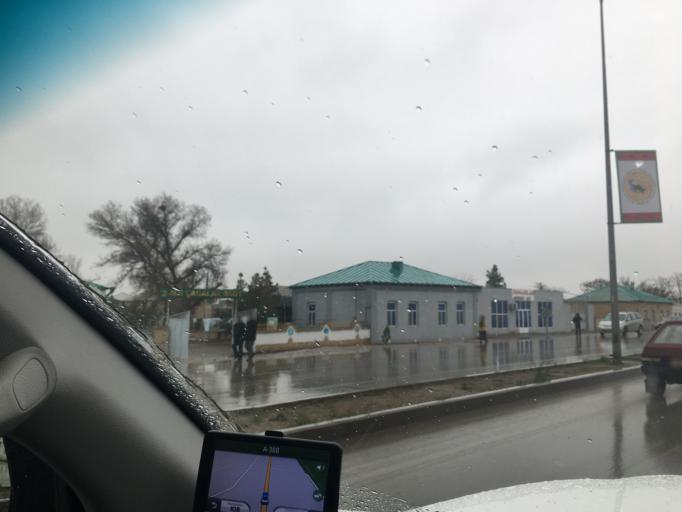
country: TM
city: Murgab
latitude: 37.4945
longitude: 61.9721
